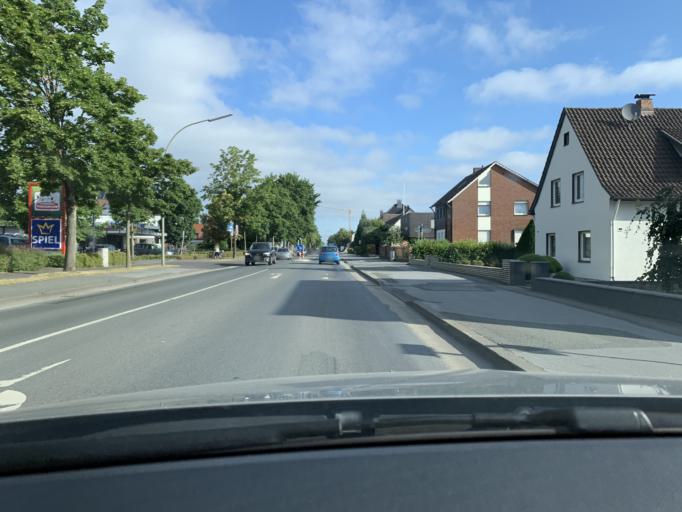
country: DE
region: North Rhine-Westphalia
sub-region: Regierungsbezirk Detmold
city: Rheda-Wiedenbruck
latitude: 51.8387
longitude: 8.3010
